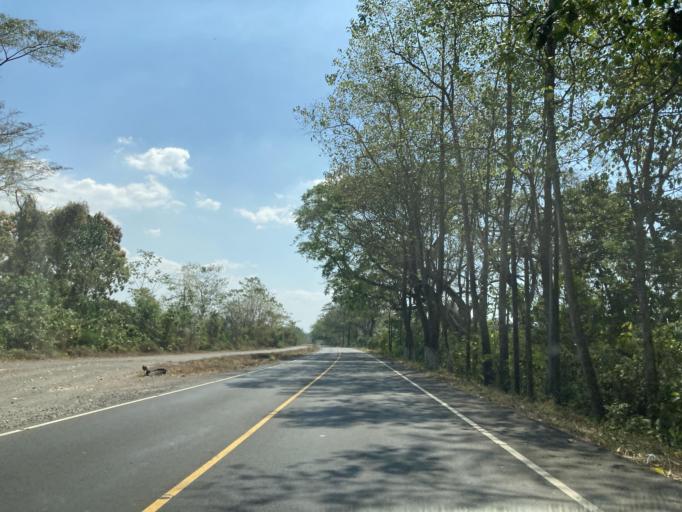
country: GT
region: Escuintla
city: Guanagazapa
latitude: 14.1785
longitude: -90.6863
